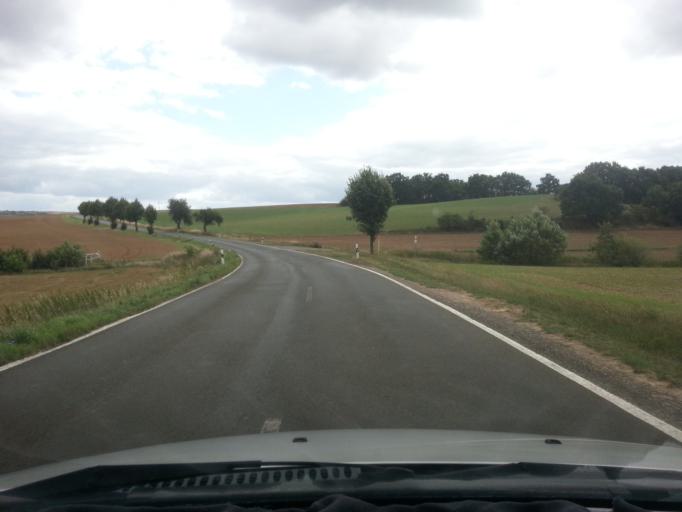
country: DE
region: Rheinland-Pfalz
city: Eisenberg
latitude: 49.5732
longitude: 8.0745
